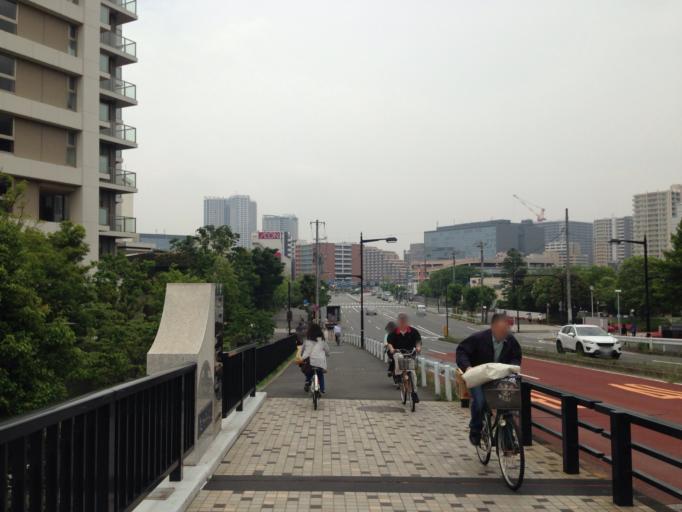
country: JP
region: Tokyo
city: Urayasu
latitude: 35.6500
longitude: 139.8051
